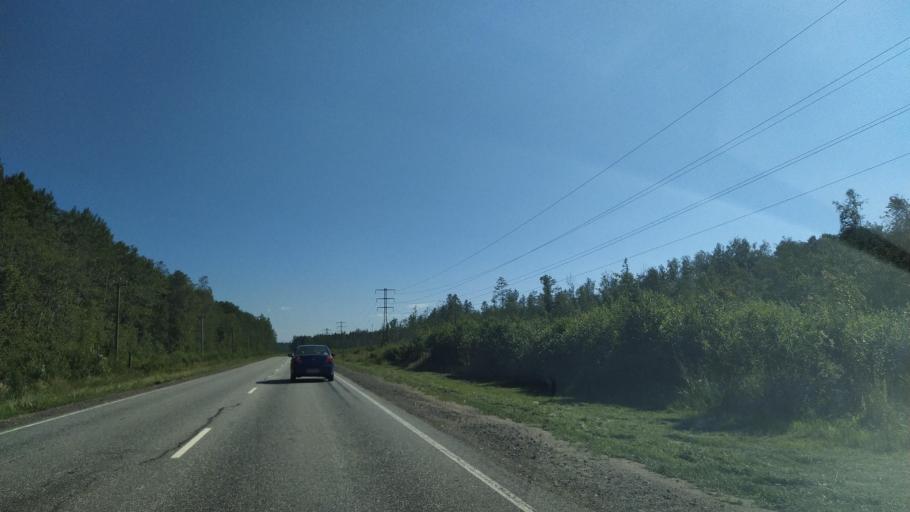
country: RU
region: Leningrad
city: Imeni Morozova
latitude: 60.0369
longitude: 31.0361
